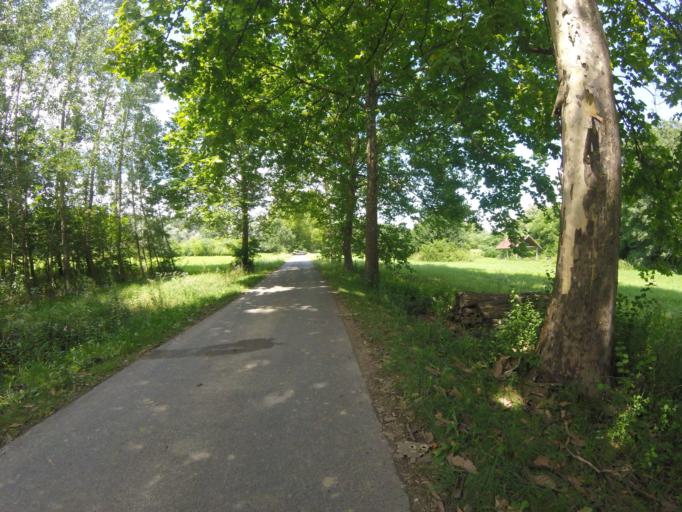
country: HR
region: Medimurska
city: Podturen
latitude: 46.5450
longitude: 16.6096
